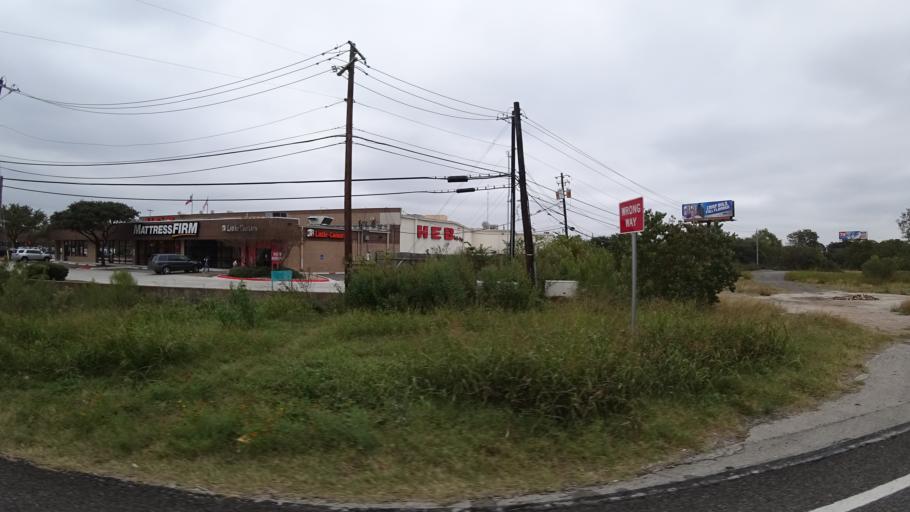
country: US
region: Texas
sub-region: Travis County
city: Barton Creek
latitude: 30.2341
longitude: -97.8740
